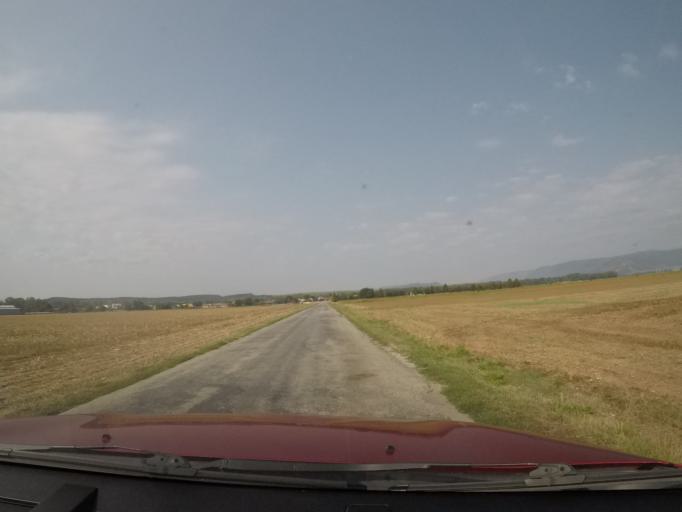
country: SK
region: Kosicky
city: Moldava nad Bodvou
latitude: 48.5814
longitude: 20.9617
